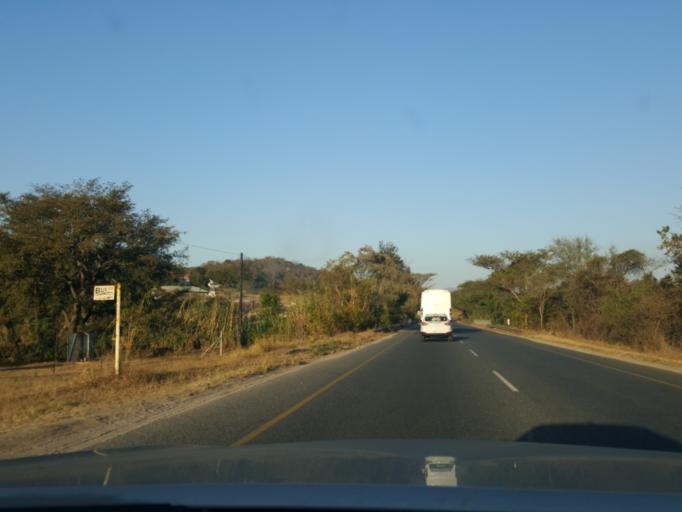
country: ZA
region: Mpumalanga
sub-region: Ehlanzeni District
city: Nelspruit
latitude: -25.4645
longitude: 31.0820
